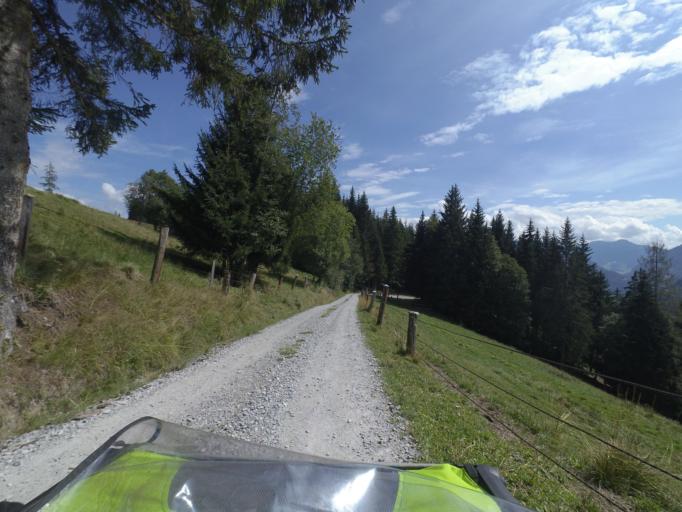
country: AT
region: Salzburg
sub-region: Politischer Bezirk Sankt Johann im Pongau
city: Muhlbach am Hochkonig
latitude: 47.3617
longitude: 13.1638
